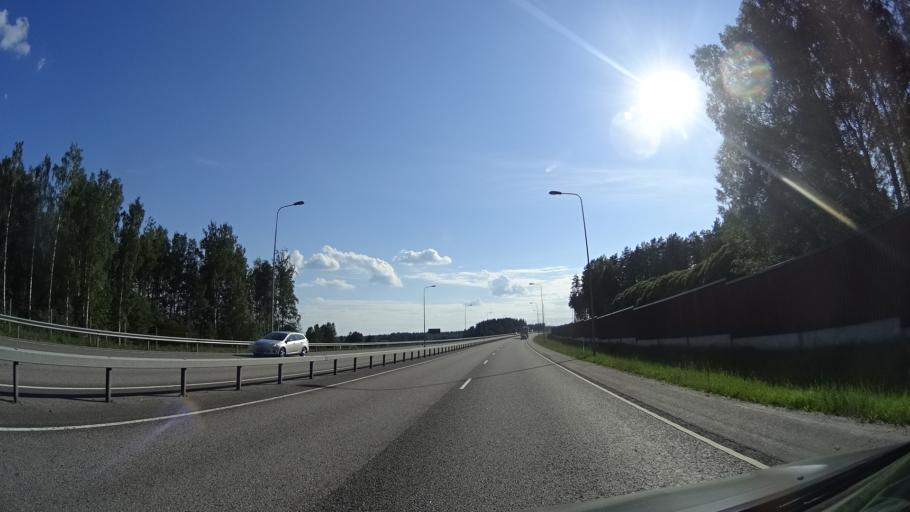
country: FI
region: South Karelia
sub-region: Imatra
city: Imatra
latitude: 61.1676
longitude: 28.6856
